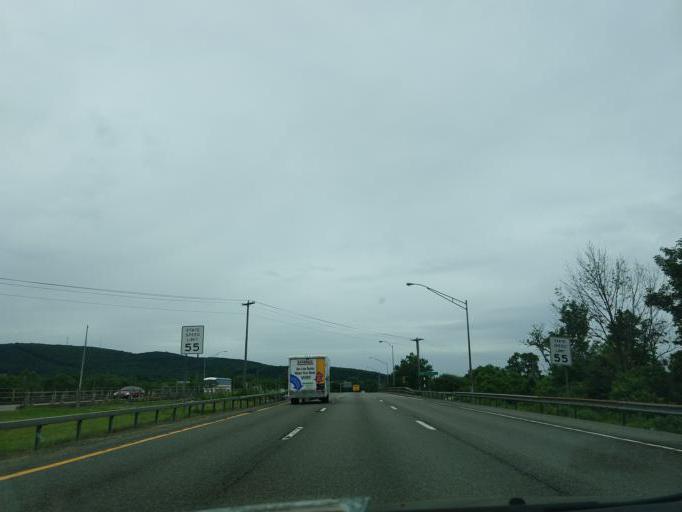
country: US
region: New York
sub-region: Broome County
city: Port Dickinson
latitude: 42.1538
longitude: -75.8979
